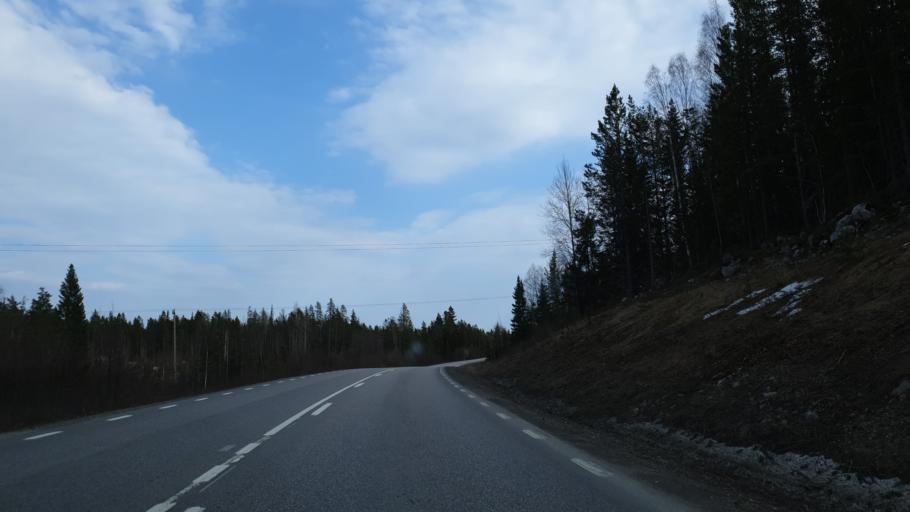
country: SE
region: Gaevleborg
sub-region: Hudiksvalls Kommun
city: Iggesund
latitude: 61.6537
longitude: 17.0236
